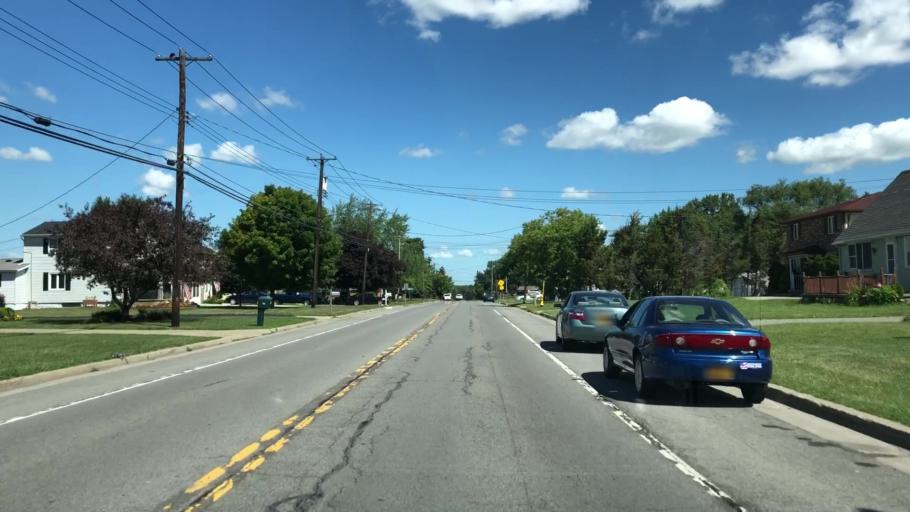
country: US
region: New York
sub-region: Erie County
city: Depew
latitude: 42.8756
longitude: -78.7090
